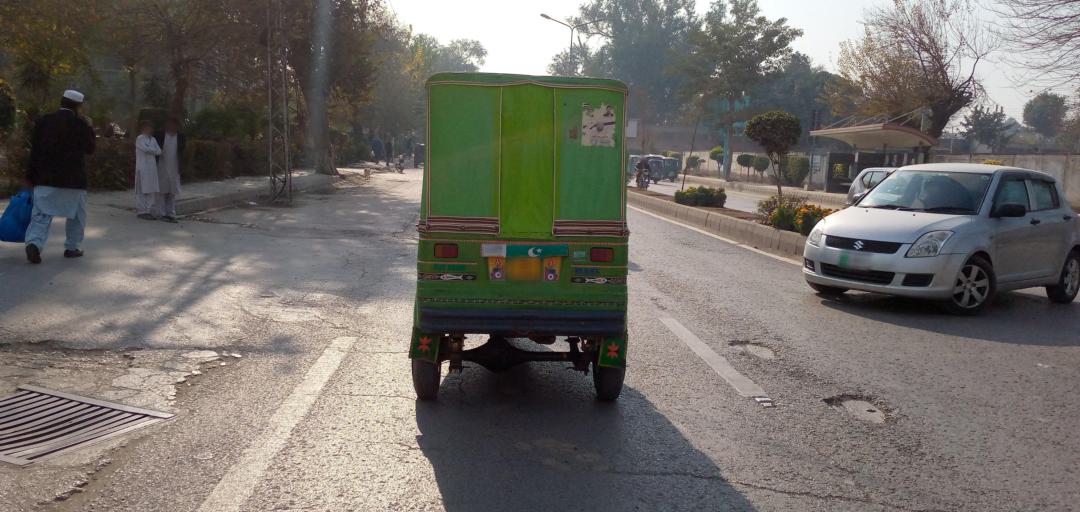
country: PK
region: Khyber Pakhtunkhwa
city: Peshawar
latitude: 33.9916
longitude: 71.5331
